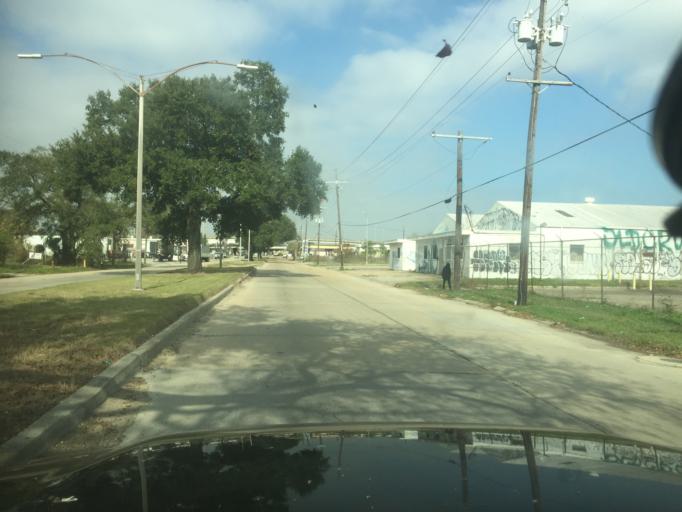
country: US
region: Louisiana
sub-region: Saint Bernard Parish
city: Arabi
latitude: 29.9996
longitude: -90.0351
